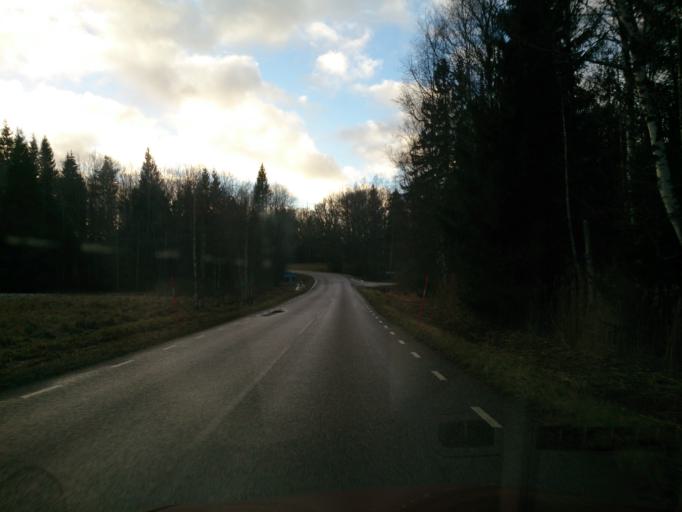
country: SE
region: OEstergoetland
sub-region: Atvidabergs Kommun
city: Atvidaberg
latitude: 58.2644
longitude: 16.0305
